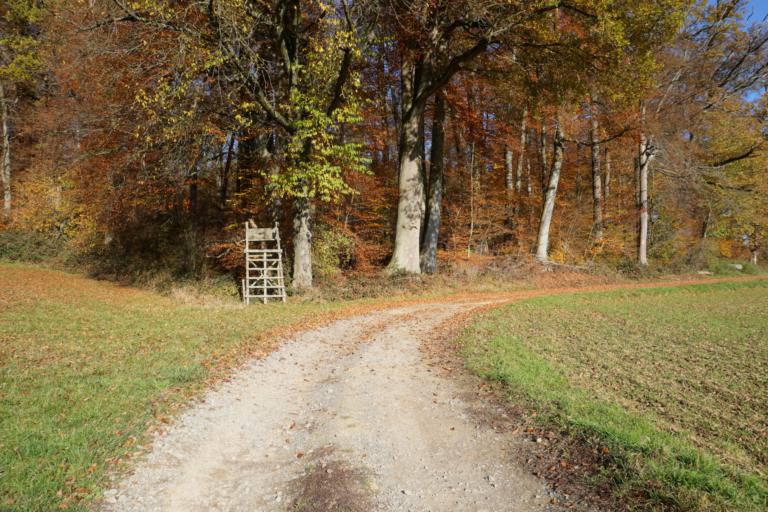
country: DE
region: Baden-Wuerttemberg
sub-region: Karlsruhe Region
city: Neunkirchen
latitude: 49.3705
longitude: 9.0047
